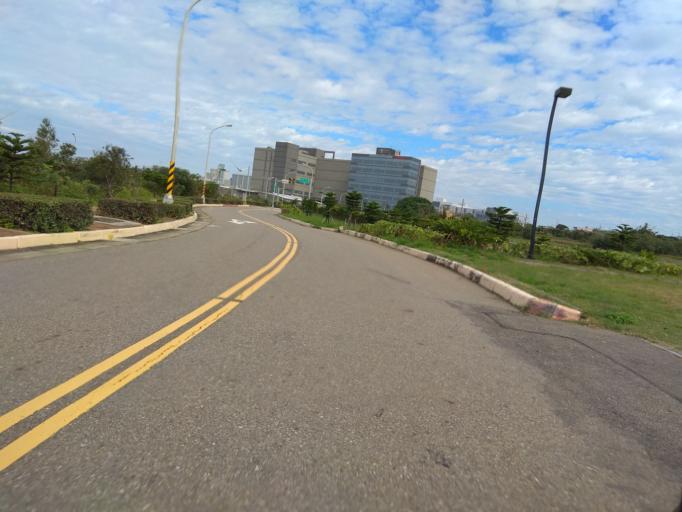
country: TW
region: Taiwan
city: Taoyuan City
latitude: 25.0459
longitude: 121.0871
